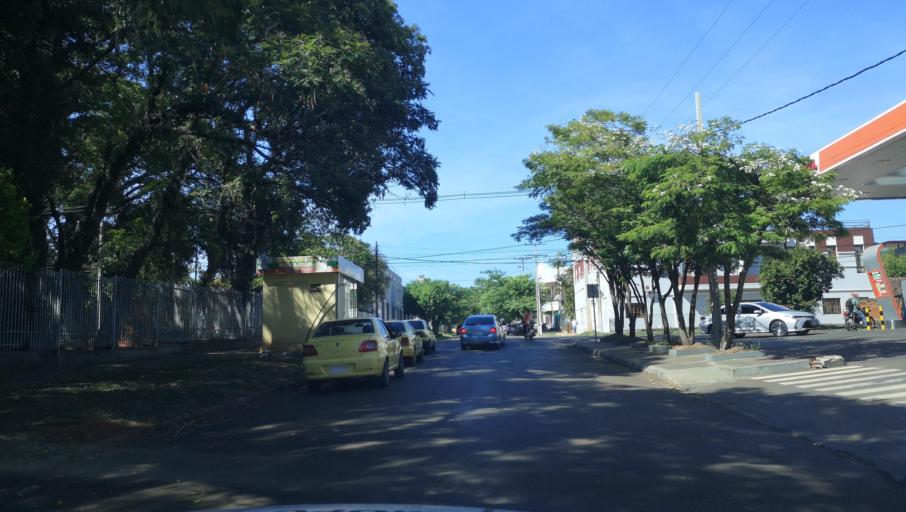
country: PY
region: Misiones
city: Santa Maria
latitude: -26.8857
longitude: -57.0227
